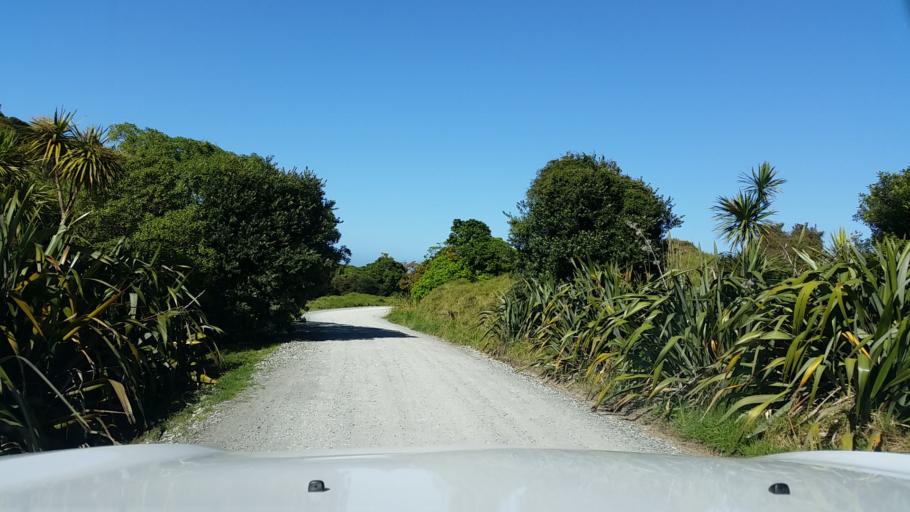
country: NZ
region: Auckland
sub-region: Auckland
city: Titirangi
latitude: -37.0385
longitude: 174.5086
